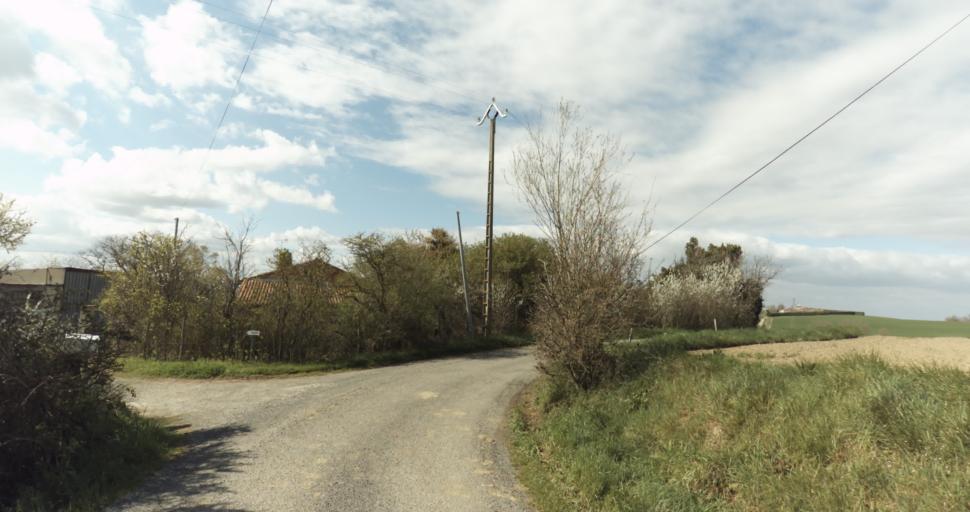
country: FR
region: Midi-Pyrenees
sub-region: Departement de la Haute-Garonne
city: Auterive
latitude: 43.3833
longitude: 1.4873
